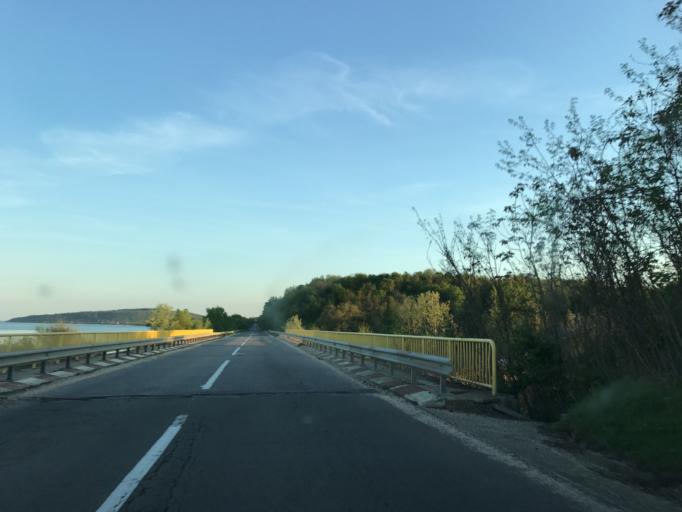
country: RO
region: Mehedinti
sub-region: Comuna Gogosu
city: Ostrovu Mare
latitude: 44.4631
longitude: 22.4509
